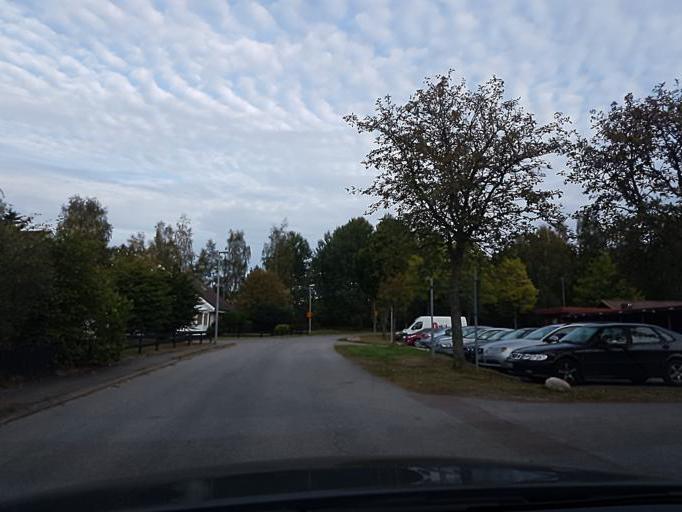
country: SE
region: Kronoberg
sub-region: Vaxjo Kommun
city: Vaexjoe
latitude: 56.8471
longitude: 14.8155
